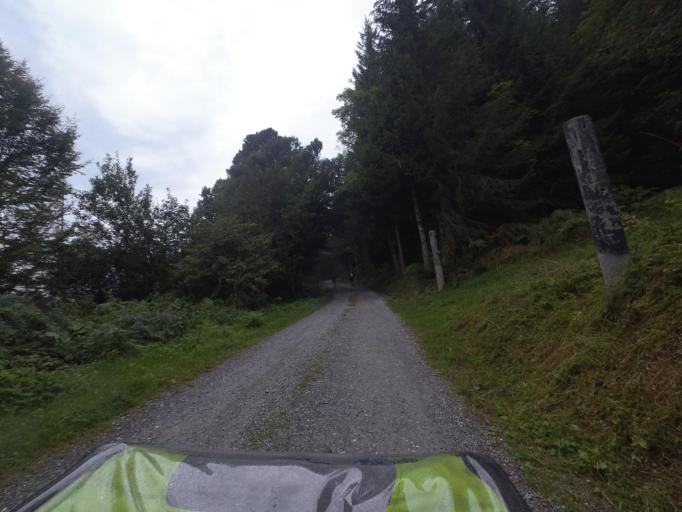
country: AT
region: Salzburg
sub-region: Politischer Bezirk Sankt Johann im Pongau
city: Sankt Veit im Pongau
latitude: 47.3606
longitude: 13.1668
